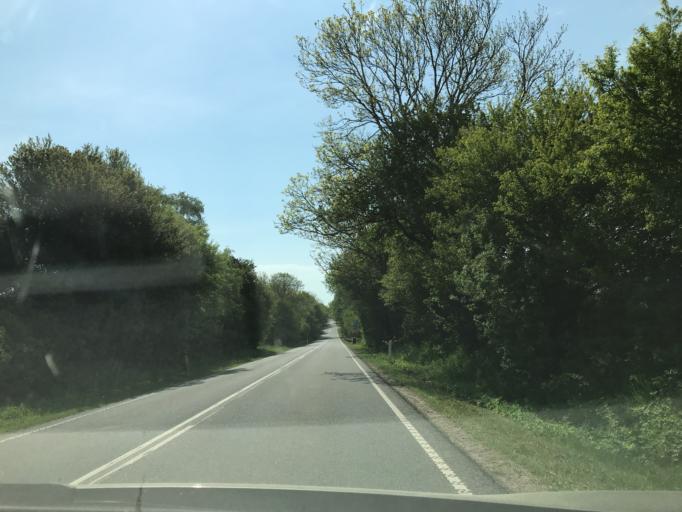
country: DK
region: South Denmark
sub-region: Middelfart Kommune
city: Ejby
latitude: 55.3743
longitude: 9.9195
